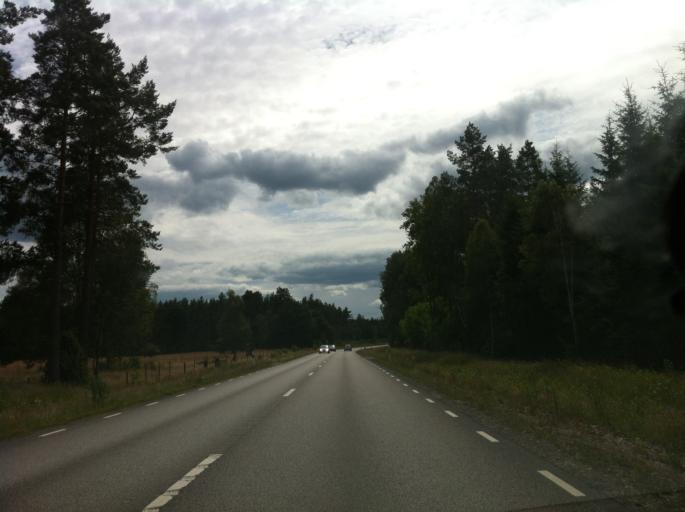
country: SE
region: Kronoberg
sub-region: Tingsryds Kommun
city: Tingsryd
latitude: 56.5269
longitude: 15.1695
